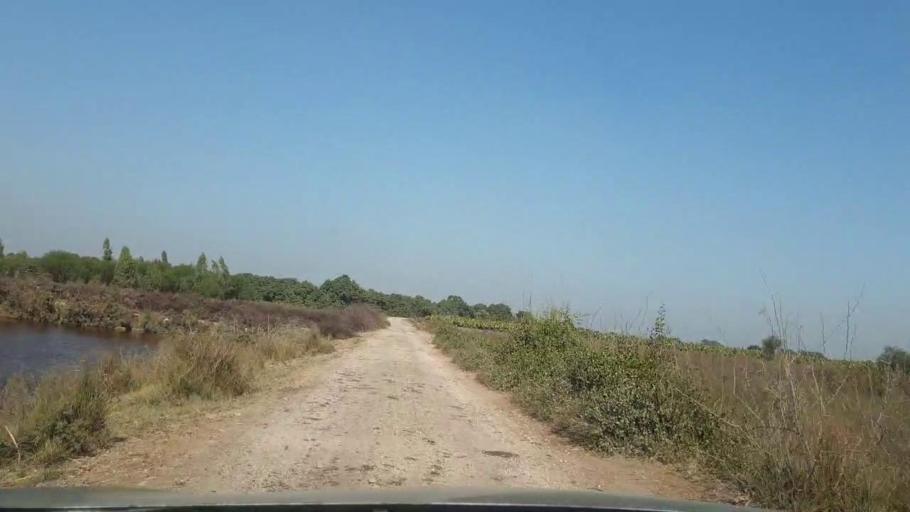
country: PK
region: Sindh
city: Tando Adam
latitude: 25.6193
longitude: 68.6462
